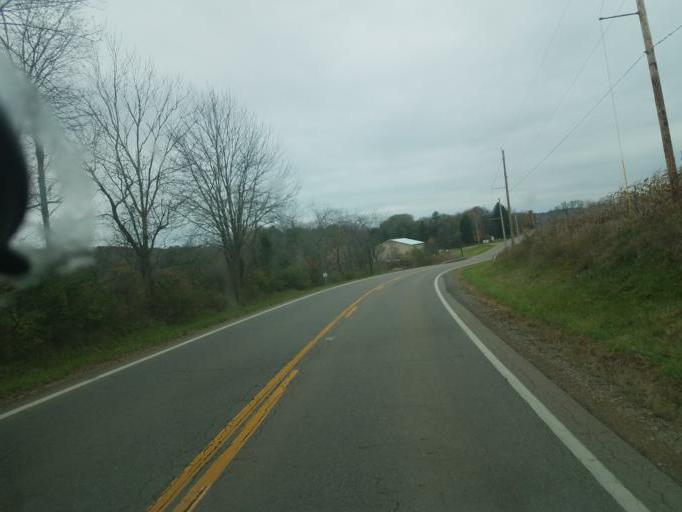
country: US
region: Ohio
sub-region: Ashland County
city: Loudonville
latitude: 40.6510
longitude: -82.1859
